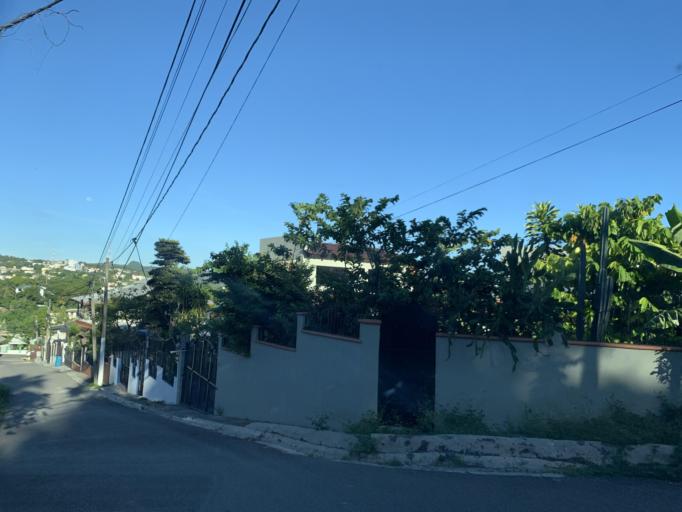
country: DO
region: Puerto Plata
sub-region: Puerto Plata
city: Puerto Plata
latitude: 19.7894
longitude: -70.6938
